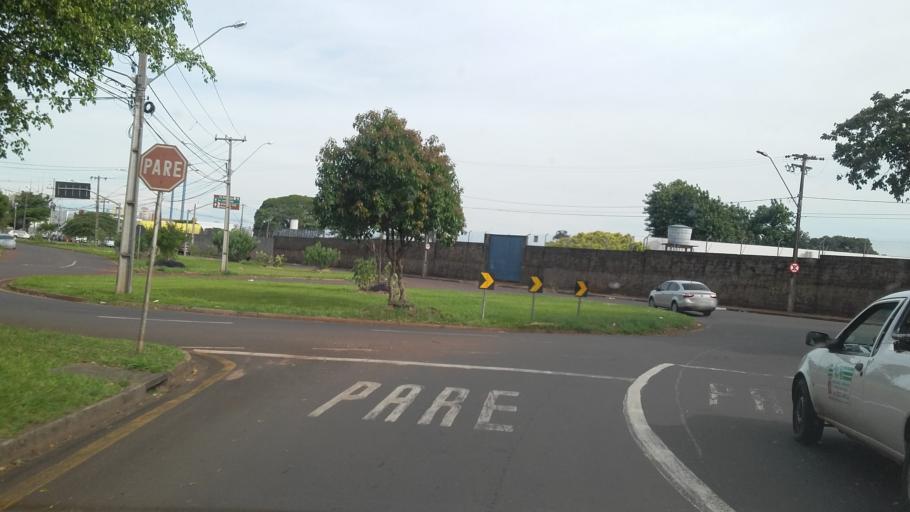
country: BR
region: Parana
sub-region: Londrina
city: Londrina
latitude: -23.2959
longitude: -51.2005
